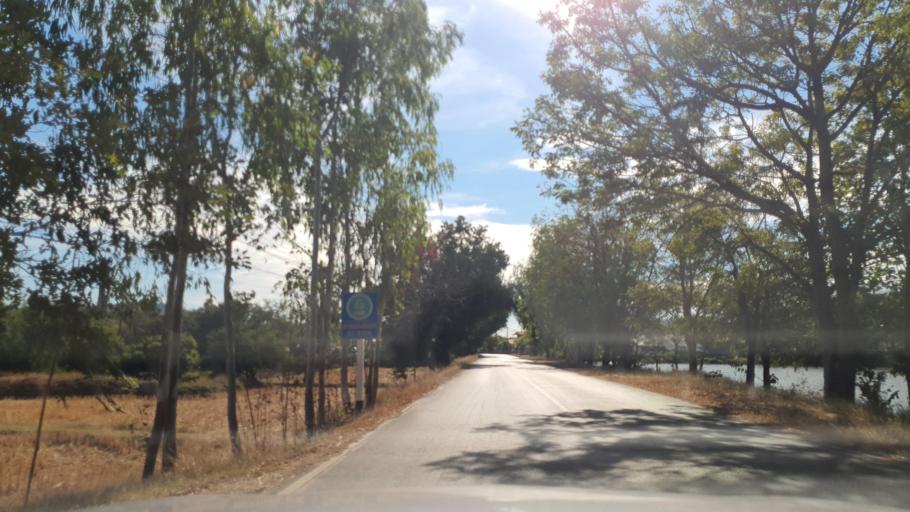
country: TH
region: Kalasin
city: Kuchinarai
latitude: 16.5942
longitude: 104.1338
